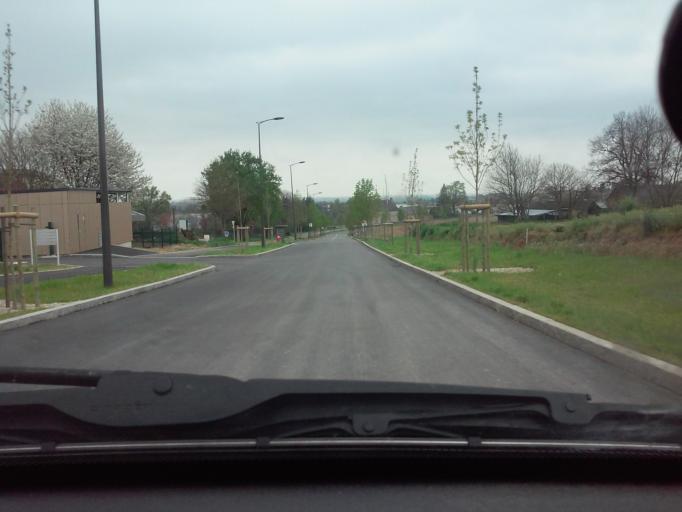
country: FR
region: Brittany
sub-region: Departement d'Ille-et-Vilaine
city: Fougeres
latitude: 48.3586
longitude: -1.1823
